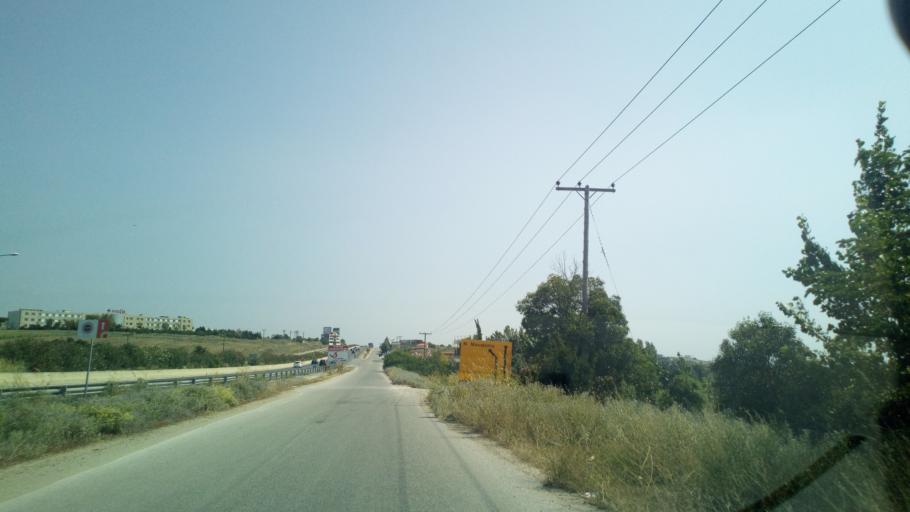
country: GR
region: Central Macedonia
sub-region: Nomos Chalkidikis
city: Lakkoma
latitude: 40.3616
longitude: 23.0506
